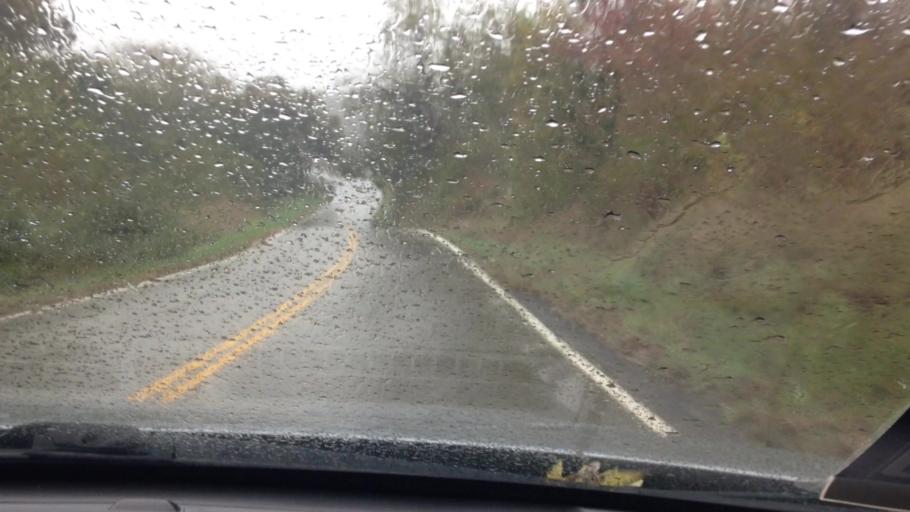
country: US
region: Kansas
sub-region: Leavenworth County
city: Lansing
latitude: 39.2030
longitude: -94.8296
